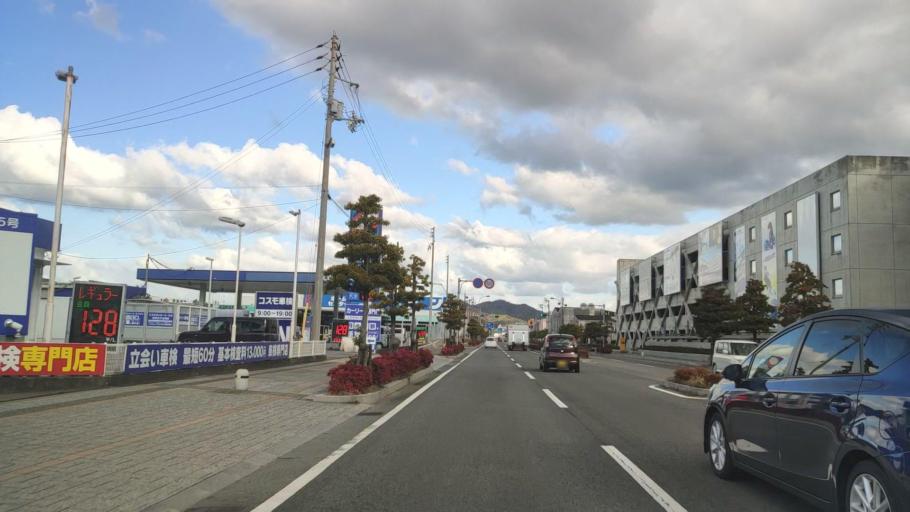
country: JP
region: Ehime
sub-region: Shikoku-chuo Shi
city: Matsuyama
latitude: 33.8501
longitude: 132.7133
